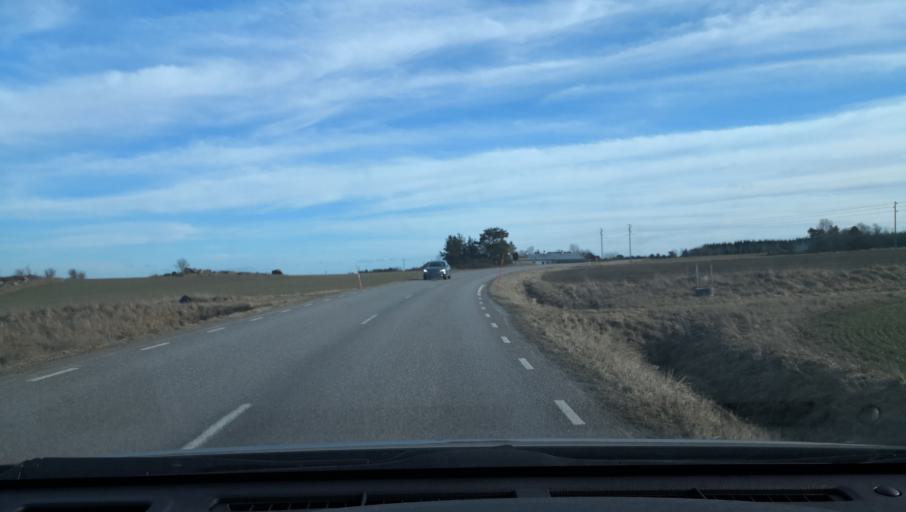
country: SE
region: Uppsala
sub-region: Enkopings Kommun
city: Enkoping
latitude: 59.6095
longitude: 17.1121
